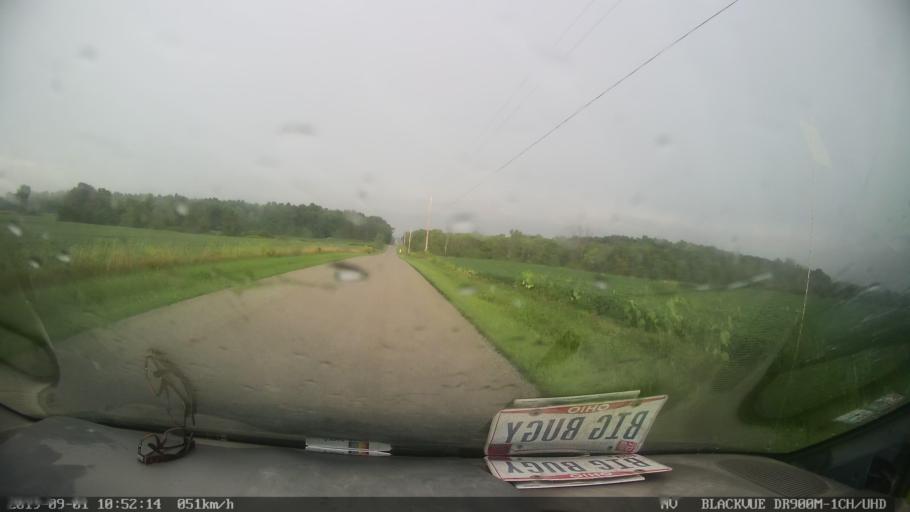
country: US
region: Ohio
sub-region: Morrow County
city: Mount Gilead
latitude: 40.6251
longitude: -82.8196
